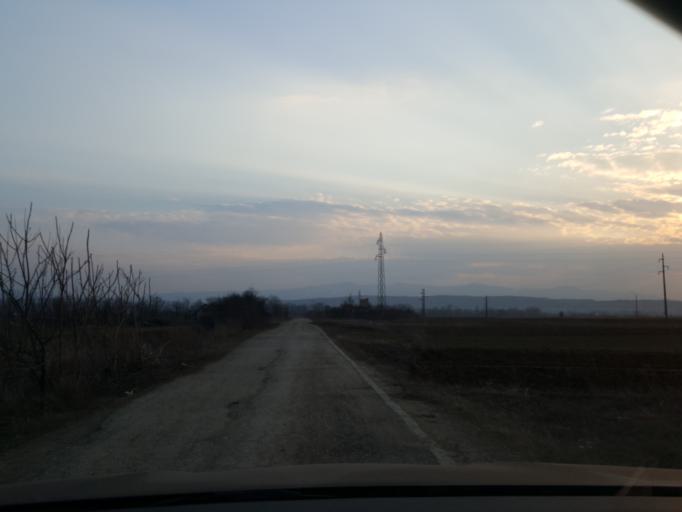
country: RS
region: Central Serbia
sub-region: Nisavski Okrug
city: Aleksinac
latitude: 43.5501
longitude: 21.6810
